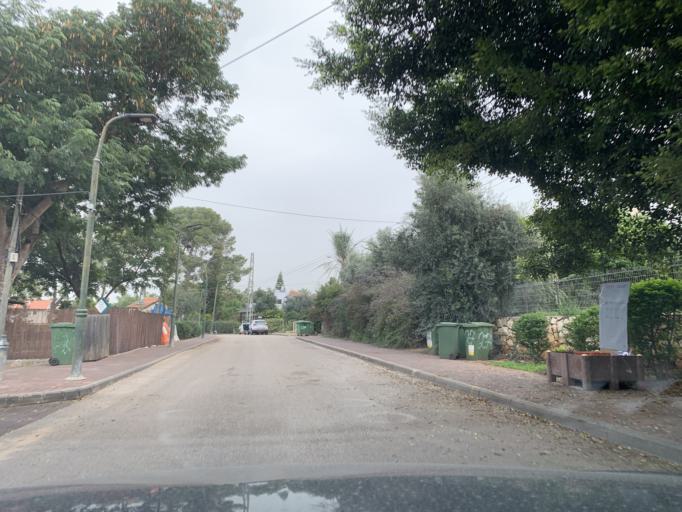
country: IL
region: Central District
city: Jaljulya
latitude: 32.1606
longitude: 34.9447
